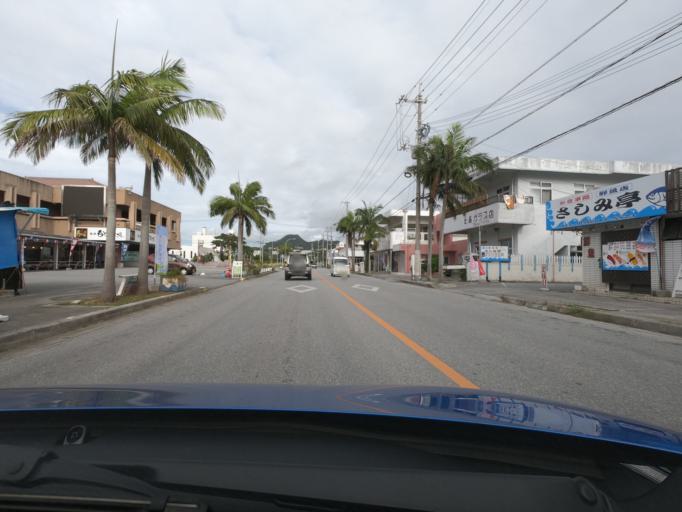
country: JP
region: Okinawa
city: Nago
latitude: 26.6574
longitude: 127.8852
